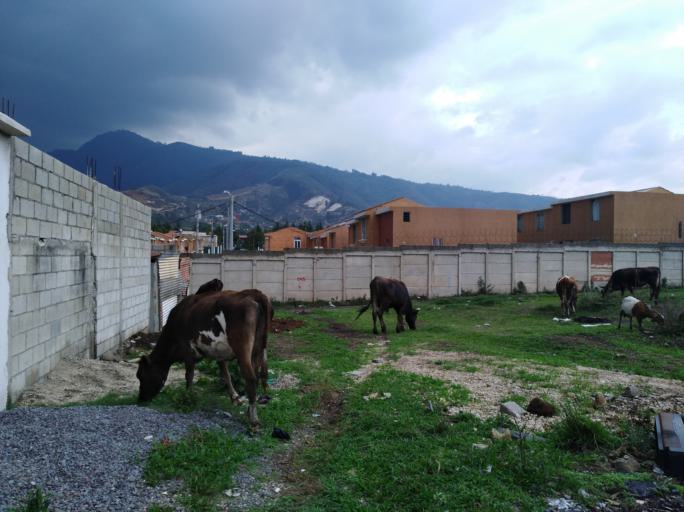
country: GT
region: Guatemala
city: Villa Nueva
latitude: 14.5251
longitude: -90.6249
